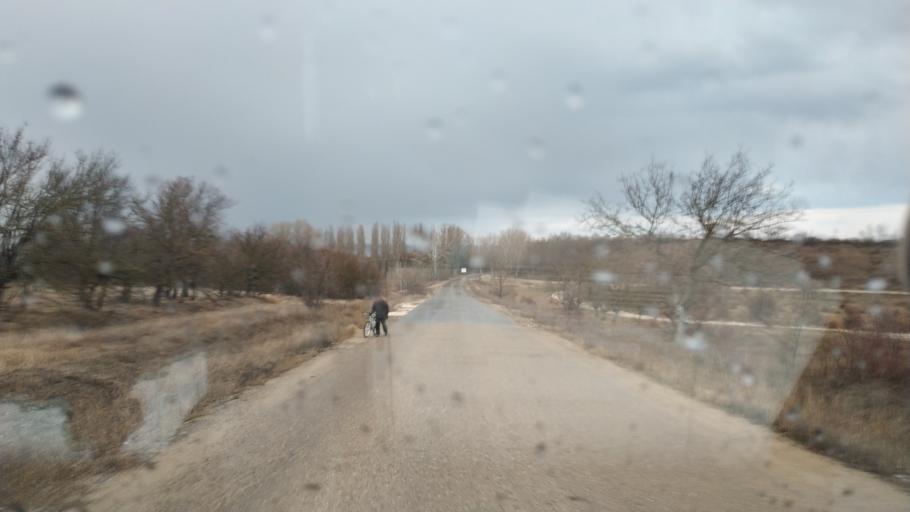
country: MD
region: Telenesti
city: Grigoriopol
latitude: 47.0769
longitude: 29.3171
